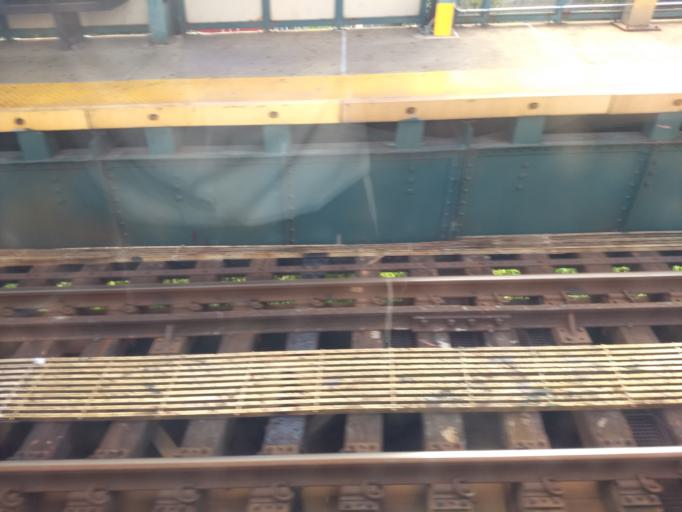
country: US
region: New York
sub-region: Kings County
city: East New York
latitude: 40.6643
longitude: -73.9007
